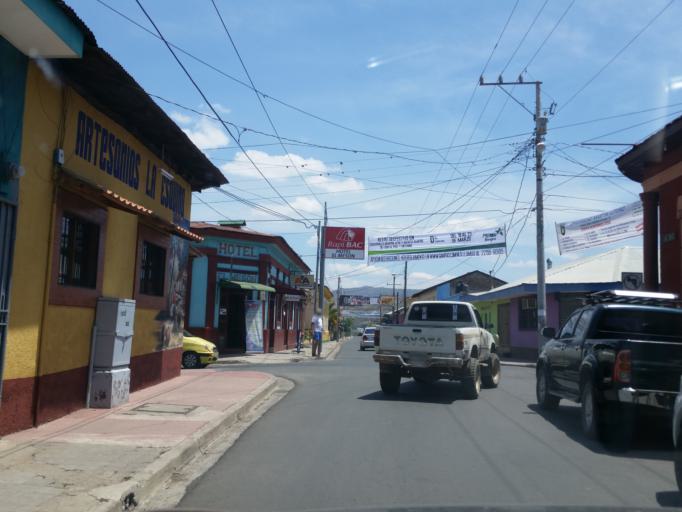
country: NI
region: Esteli
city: Esteli
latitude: 13.0942
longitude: -86.3562
